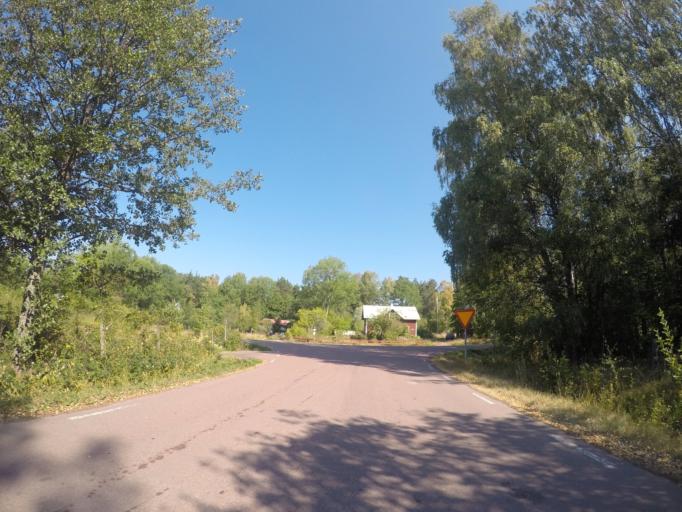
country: AX
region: Alands landsbygd
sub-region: Jomala
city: Jomala
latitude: 60.2112
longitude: 19.9732
